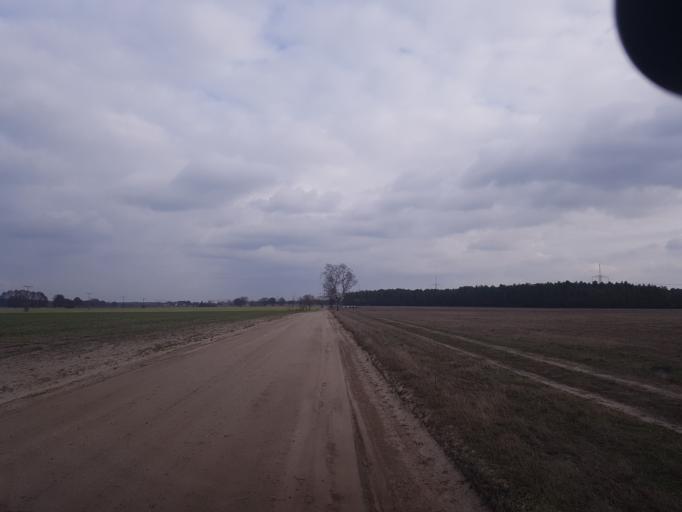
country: DE
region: Brandenburg
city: Sonnewalde
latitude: 51.6634
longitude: 13.6555
